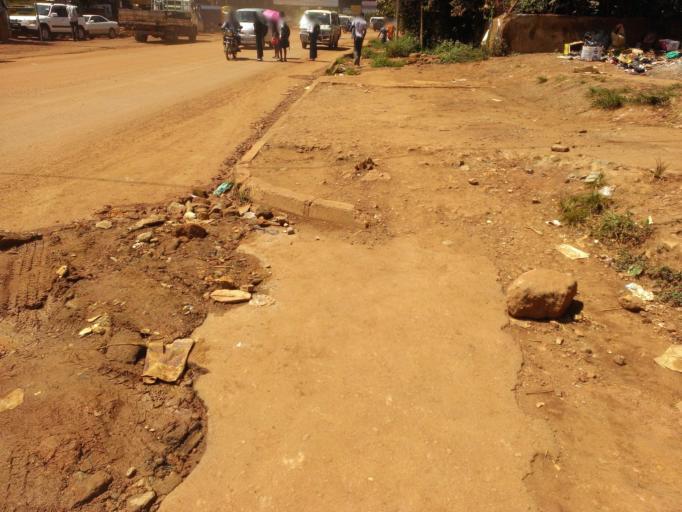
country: UG
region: Central Region
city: Kampala Central Division
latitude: 0.3273
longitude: 32.5642
